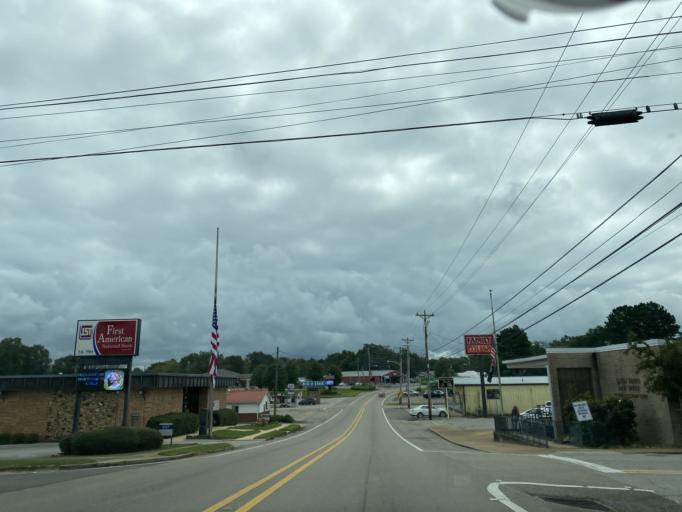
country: US
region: Mississippi
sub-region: Tishomingo County
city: Belmont
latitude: 34.5087
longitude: -88.2083
